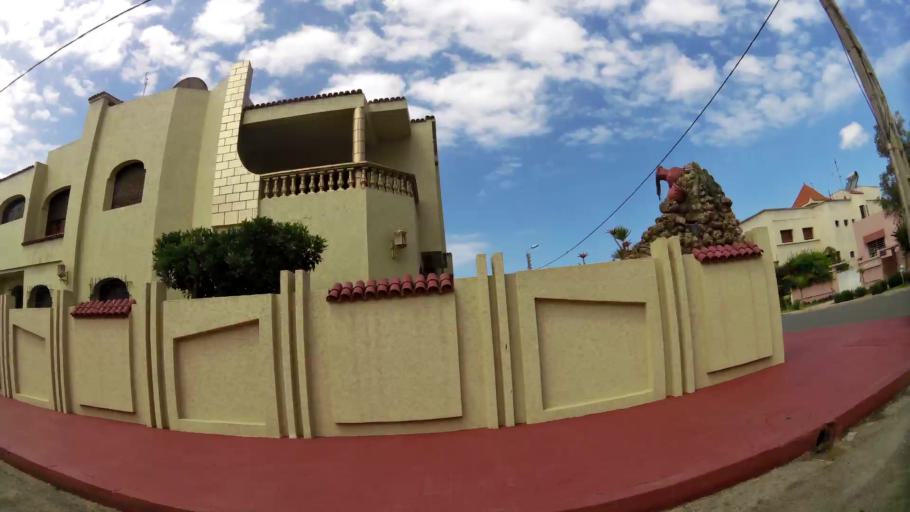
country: MA
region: Gharb-Chrarda-Beni Hssen
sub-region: Kenitra Province
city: Kenitra
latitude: 34.2496
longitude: -6.5974
